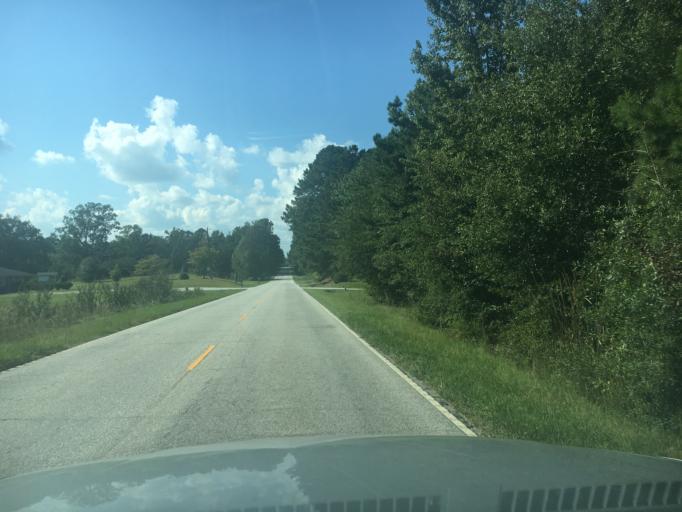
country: US
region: South Carolina
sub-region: Greenwood County
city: Greenwood
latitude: 34.2913
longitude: -82.2102
